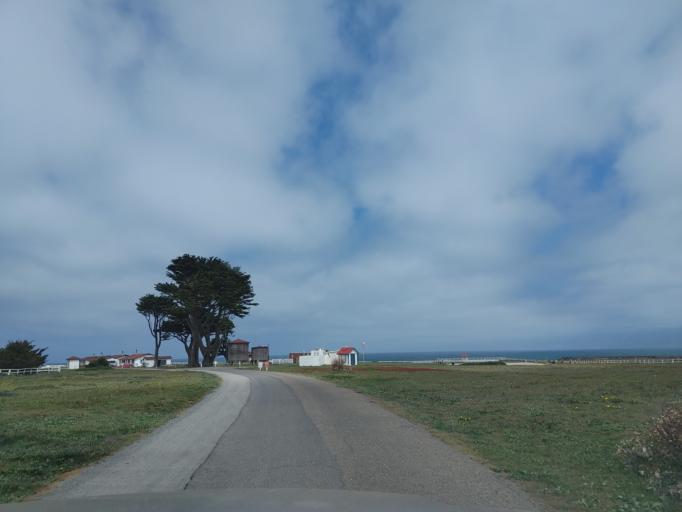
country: US
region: California
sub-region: Sonoma County
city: Sea Ranch
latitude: 38.9520
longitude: -123.7374
